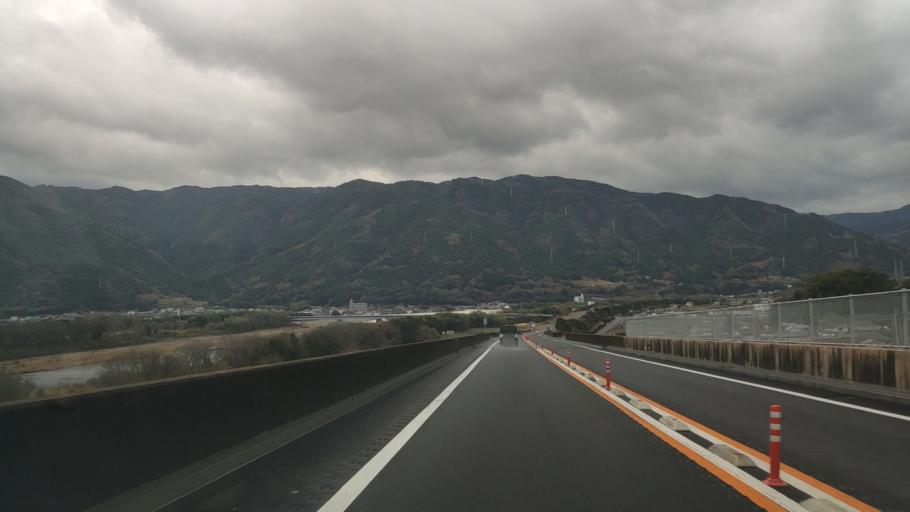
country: JP
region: Tokushima
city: Ikedacho
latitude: 34.0478
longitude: 133.9139
